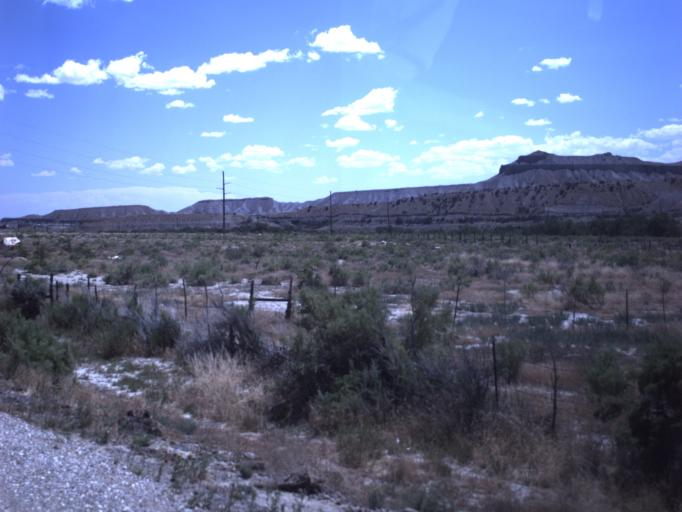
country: US
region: Utah
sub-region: Emery County
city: Orangeville
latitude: 39.2568
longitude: -111.1012
